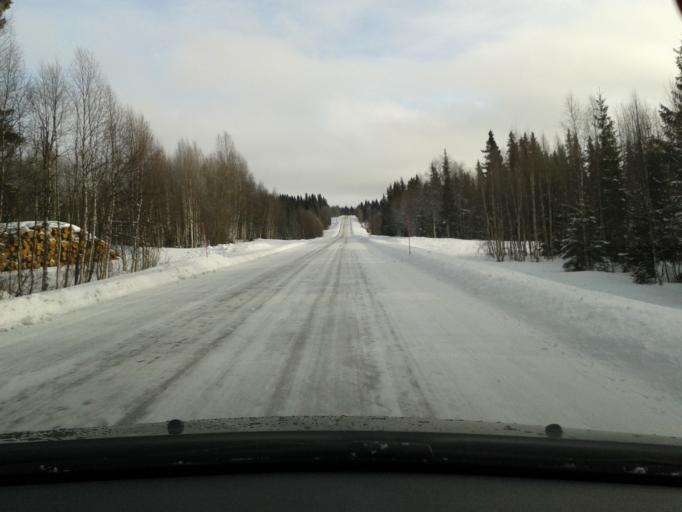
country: SE
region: Vaesterbotten
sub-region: Vilhelmina Kommun
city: Sjoberg
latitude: 64.7958
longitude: 16.0566
